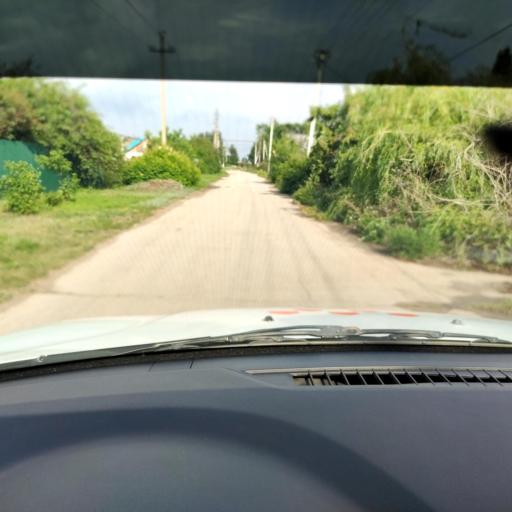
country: RU
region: Samara
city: Podstepki
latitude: 53.6140
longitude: 49.0368
